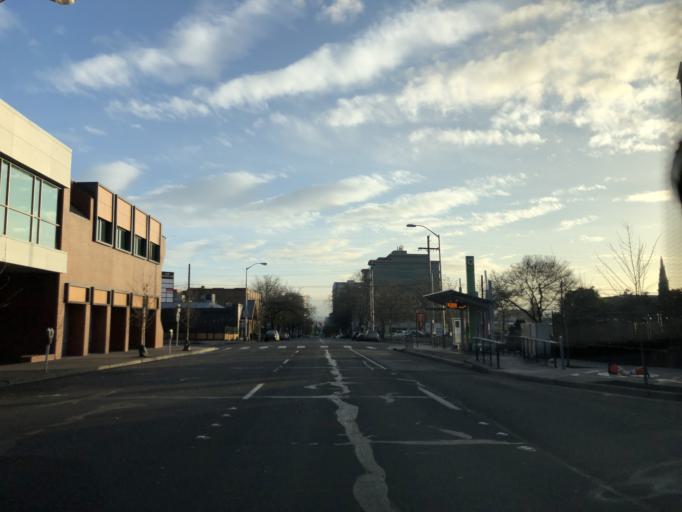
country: US
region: Washington
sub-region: Clark County
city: Vancouver
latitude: 45.6310
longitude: -122.6727
